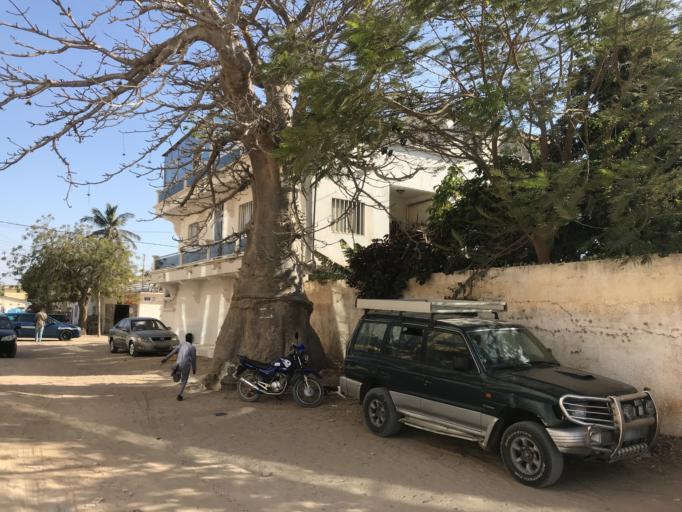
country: SN
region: Saint-Louis
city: Saint-Louis
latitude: 16.0211
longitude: -16.4897
